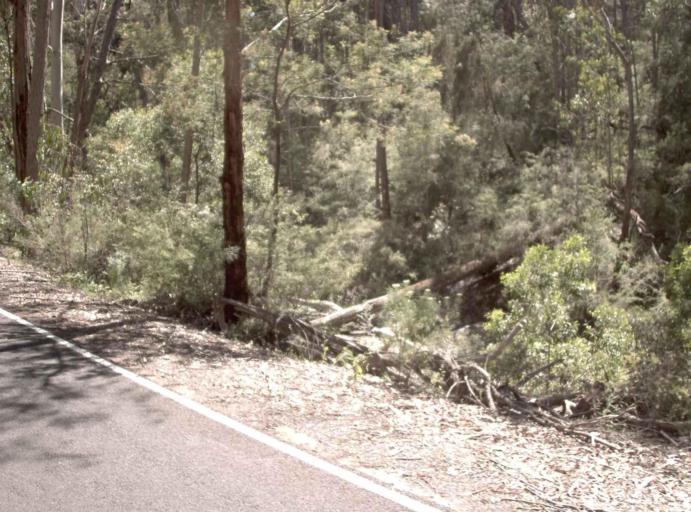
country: AU
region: Victoria
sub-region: East Gippsland
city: Lakes Entrance
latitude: -37.3681
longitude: 148.2186
